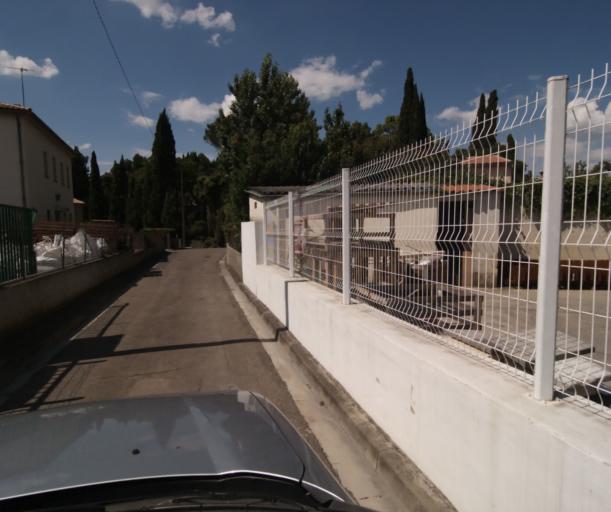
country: FR
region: Languedoc-Roussillon
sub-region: Departement de l'Aude
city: Limoux
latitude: 43.0562
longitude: 2.2125
